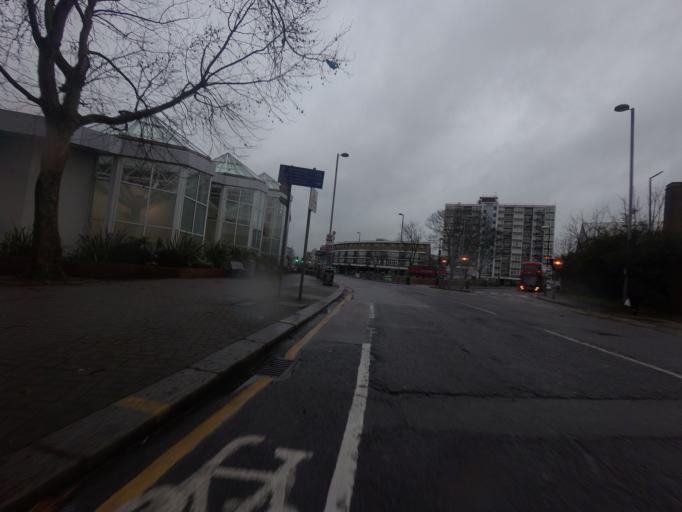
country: GB
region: England
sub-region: Greater London
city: Walthamstow
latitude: 51.5734
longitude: -0.0089
